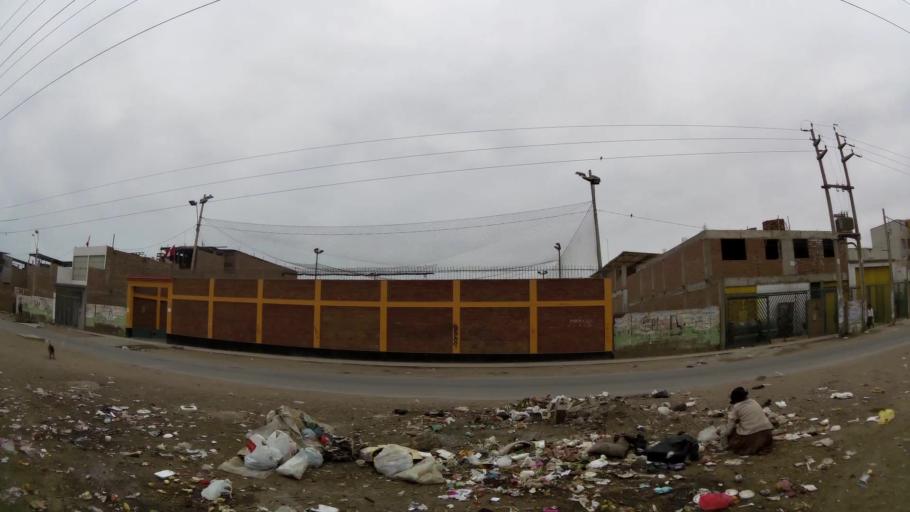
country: PE
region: Lima
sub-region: Lima
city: Surco
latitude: -12.2004
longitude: -76.9661
